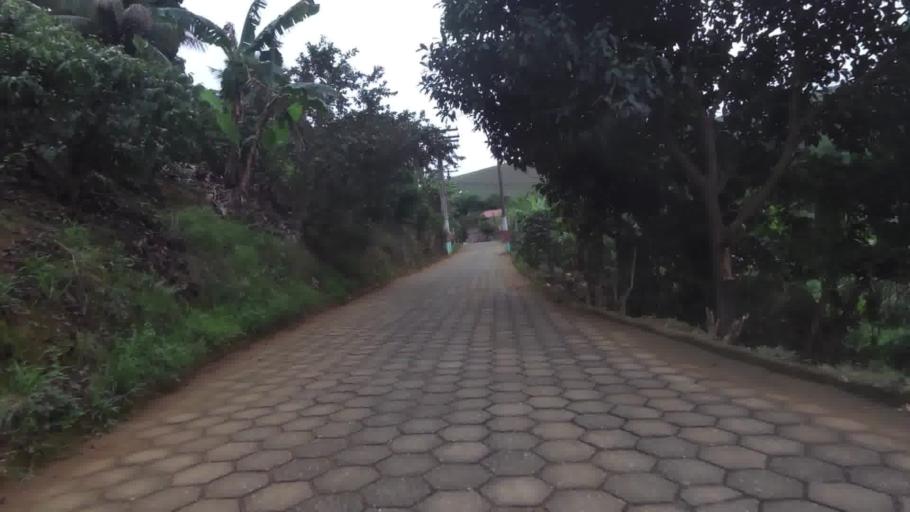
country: BR
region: Espirito Santo
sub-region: Iconha
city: Iconha
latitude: -20.7741
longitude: -40.8287
